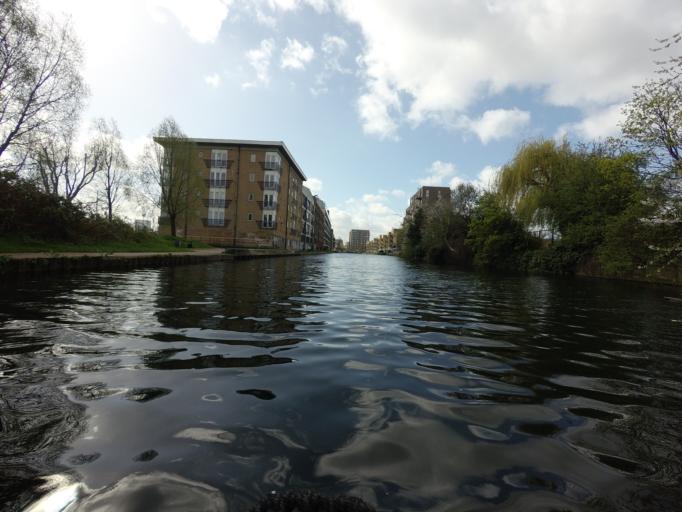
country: GB
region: England
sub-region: Greater London
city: Poplar
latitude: 51.5214
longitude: -0.0364
